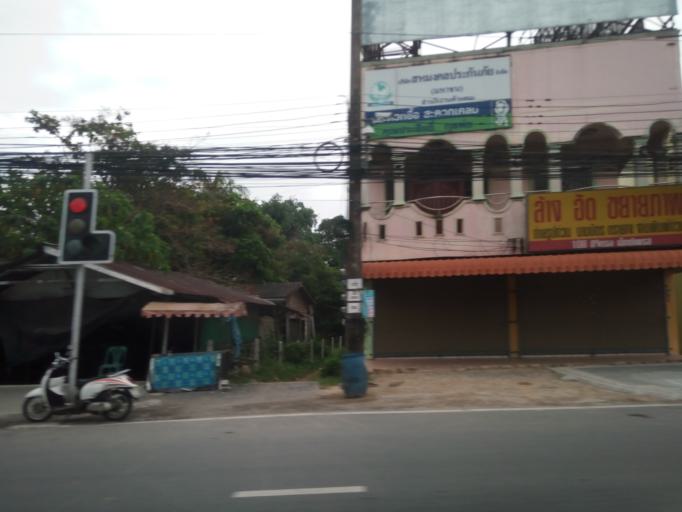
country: TH
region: Phuket
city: Ban Ko Kaeo
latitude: 7.9614
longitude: 98.3805
